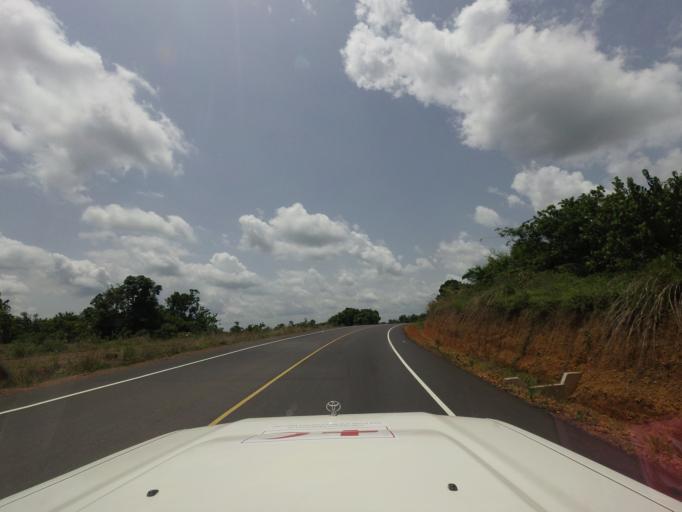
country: LR
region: Margibi
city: Kakata
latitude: 6.4981
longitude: -10.3913
